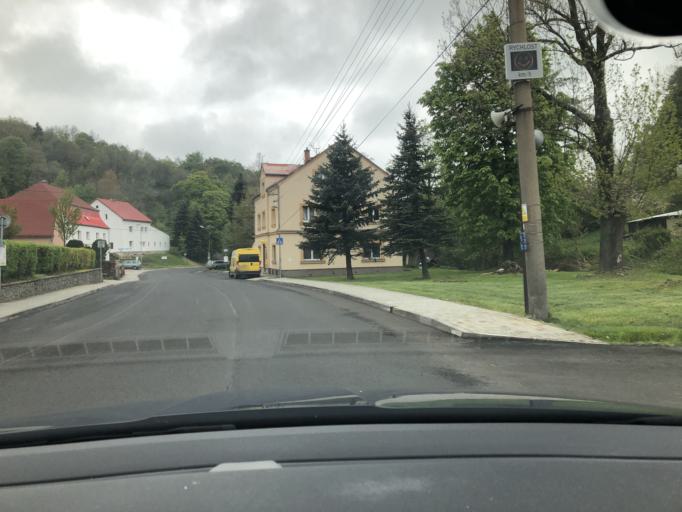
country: CZ
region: Ustecky
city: Libouchec
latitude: 50.7901
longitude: 13.9758
